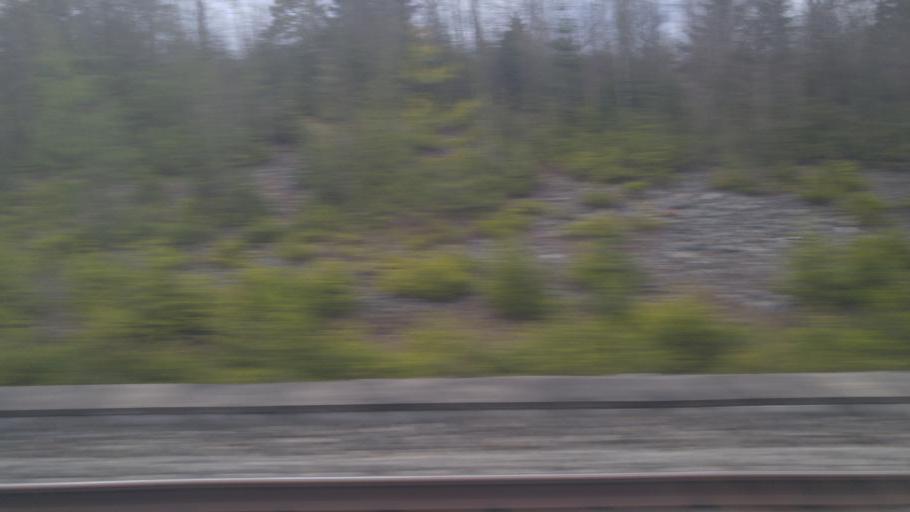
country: NO
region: Akershus
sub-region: Sorum
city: Frogner
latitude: 60.0289
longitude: 11.1246
